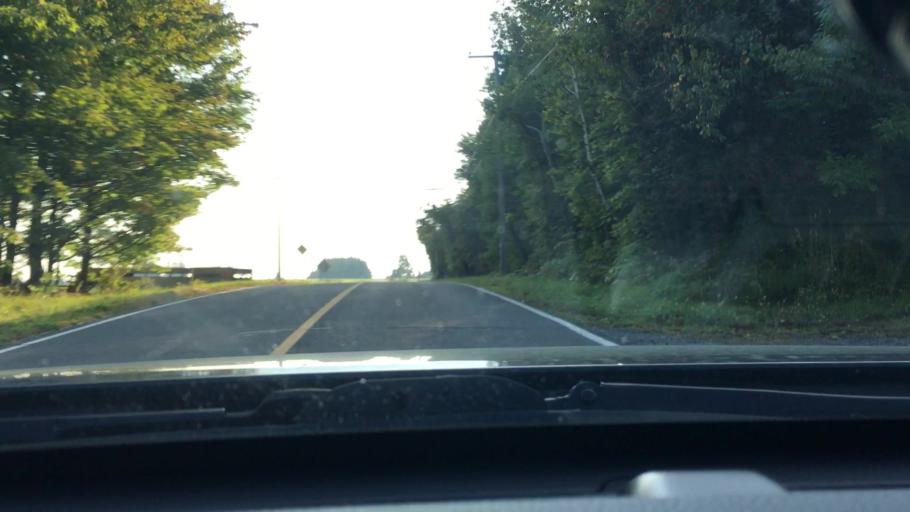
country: CA
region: Quebec
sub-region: Monteregie
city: Waterloo
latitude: 45.3558
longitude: -72.4987
